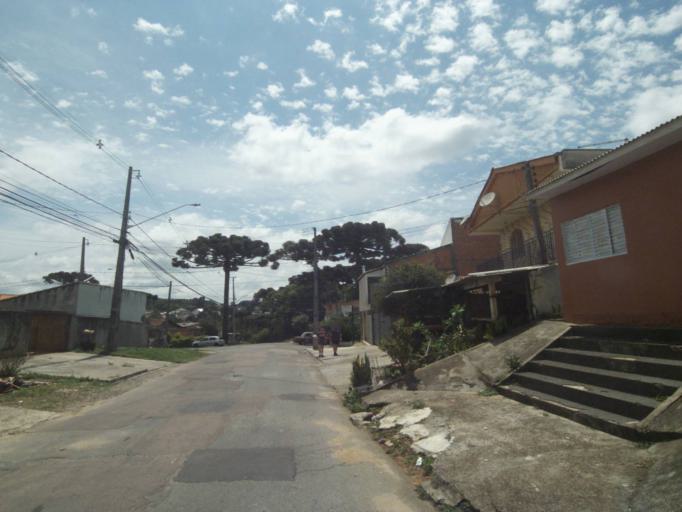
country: BR
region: Parana
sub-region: Curitiba
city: Curitiba
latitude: -25.4576
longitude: -49.3437
